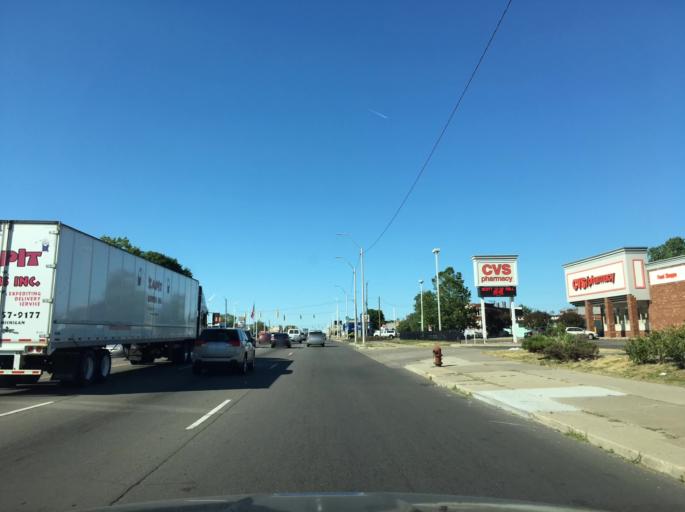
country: US
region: Michigan
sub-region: Wayne County
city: Hamtramck
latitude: 42.4036
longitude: -82.9982
